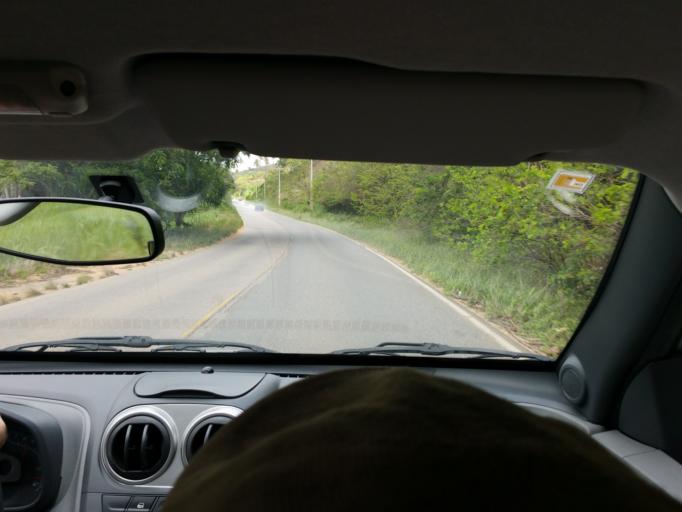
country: BR
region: Pernambuco
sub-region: Sirinhaem
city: Sirinhaem
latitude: -8.6320
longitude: -35.1198
